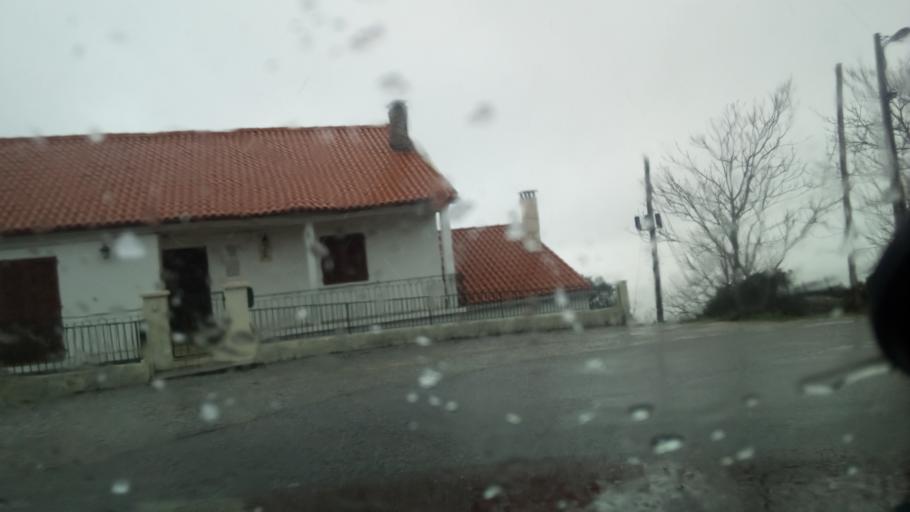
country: PT
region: Guarda
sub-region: Fornos de Algodres
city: Fornos de Algodres
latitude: 40.5404
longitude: -7.4644
